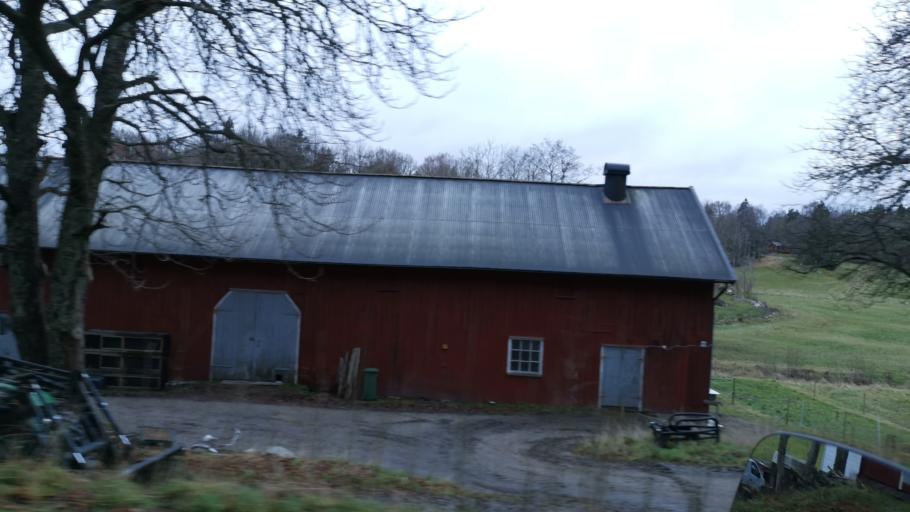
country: SE
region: Vaestra Goetaland
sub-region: Orust
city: Henan
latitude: 58.2268
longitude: 11.7012
